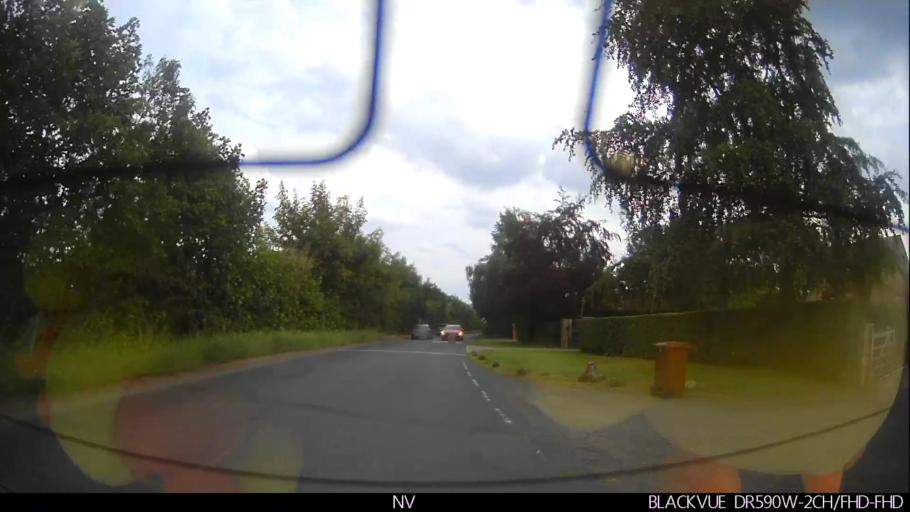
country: GB
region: England
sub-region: City of York
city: Holtby
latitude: 54.0486
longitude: -0.9593
